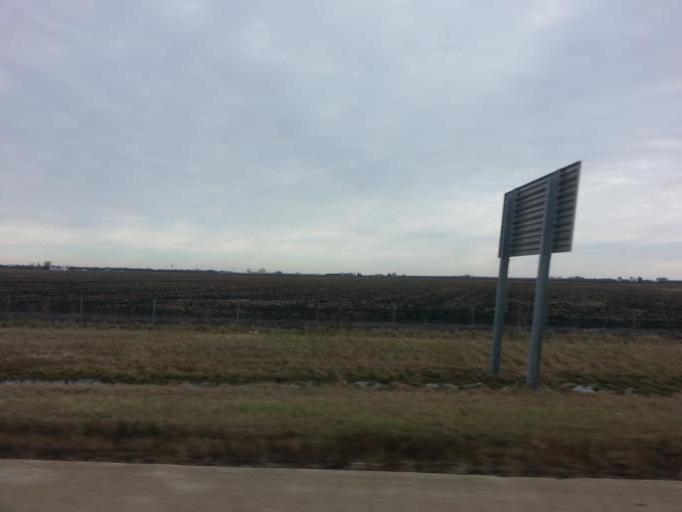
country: US
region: Illinois
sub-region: Woodford County
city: El Paso
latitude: 40.7135
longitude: -89.0323
